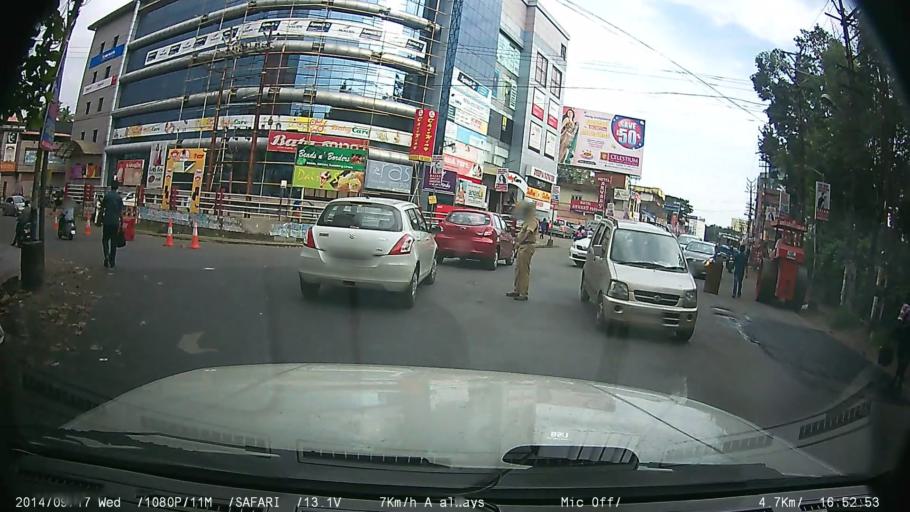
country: IN
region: Kerala
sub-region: Pattanamtitta
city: Tiruvalla
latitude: 9.3890
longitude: 76.5749
